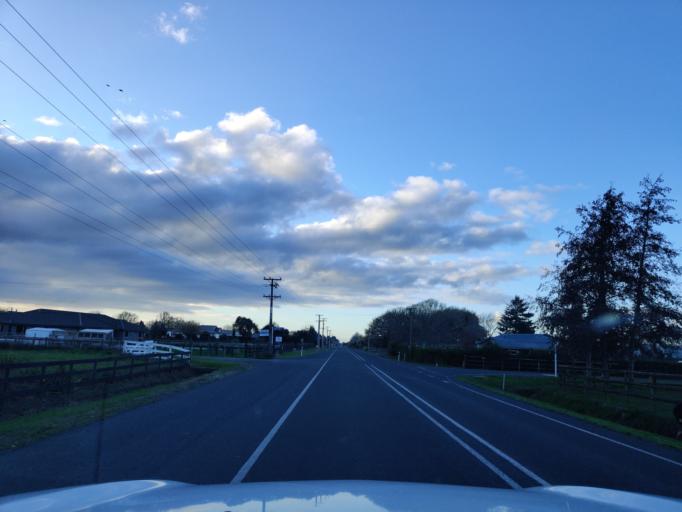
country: NZ
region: Waikato
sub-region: Waipa District
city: Cambridge
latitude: -37.8813
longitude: 175.4389
